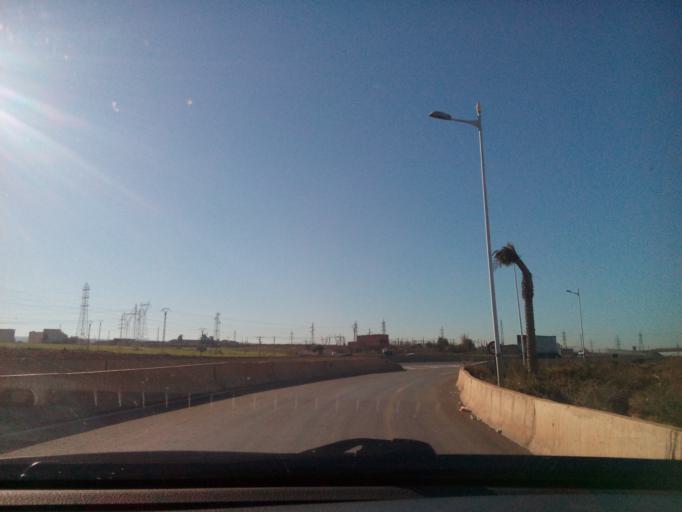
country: DZ
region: Chlef
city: Oued Sly
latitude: 36.0923
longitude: 1.2020
